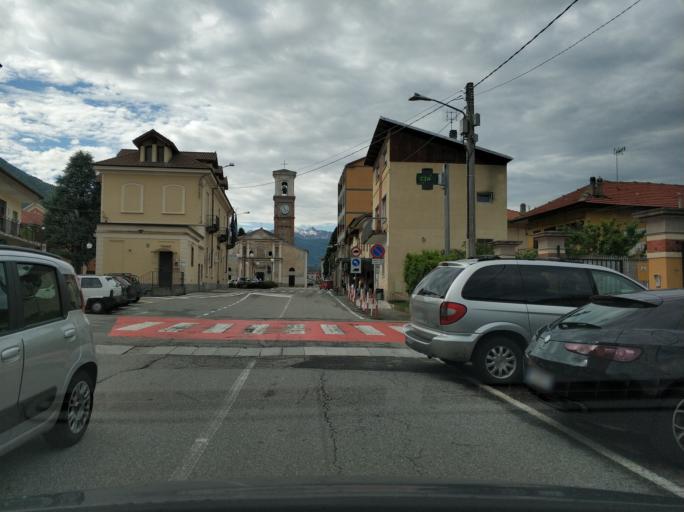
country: IT
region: Piedmont
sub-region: Provincia di Torino
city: Cafasse
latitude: 45.2443
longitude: 7.5187
